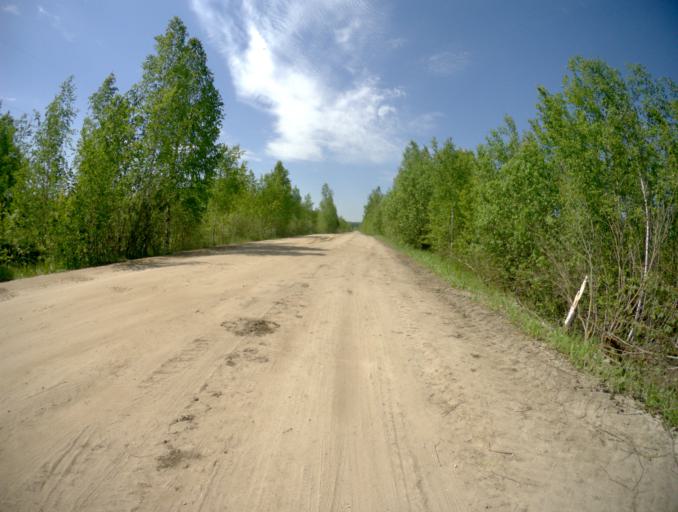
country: RU
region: Vladimir
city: Gusevskiy
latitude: 55.6900
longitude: 40.5300
